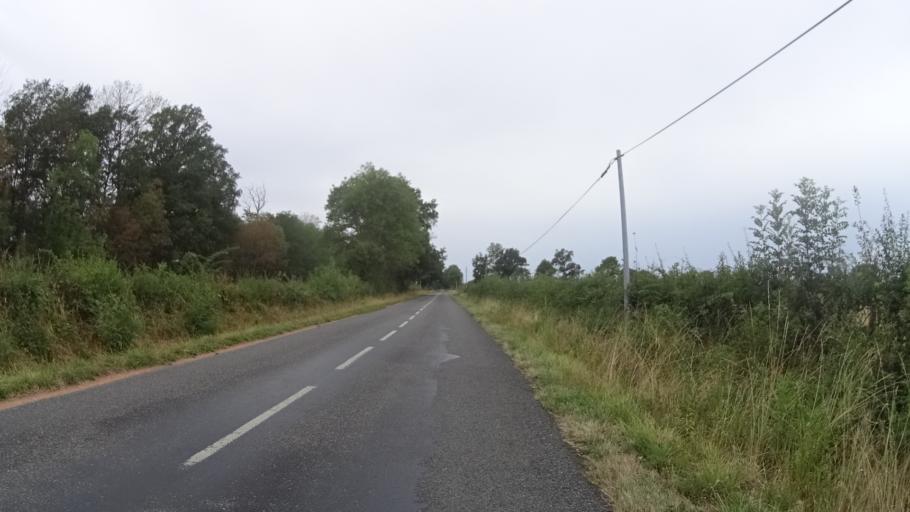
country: FR
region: Bourgogne
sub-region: Departement de la Nievre
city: Decize
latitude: 46.7921
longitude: 3.5110
